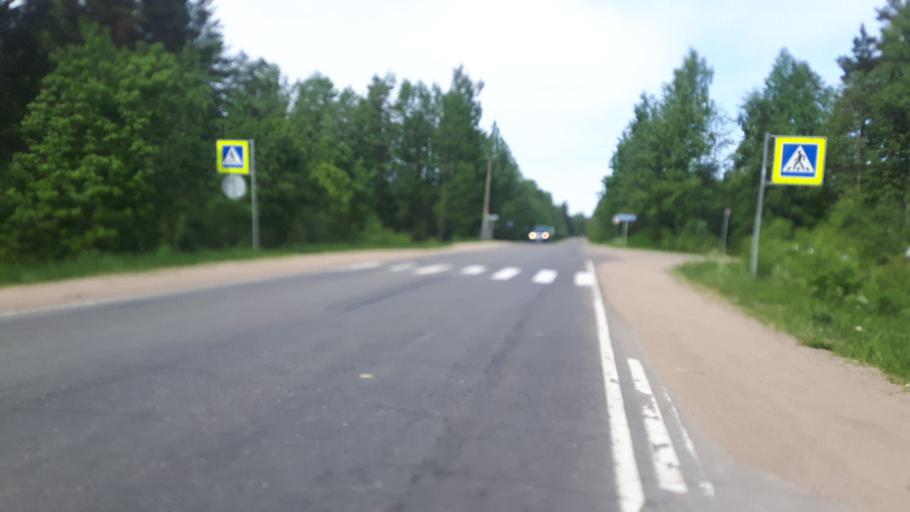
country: RU
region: Leningrad
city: Ust'-Luga
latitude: 59.6453
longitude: 28.2688
